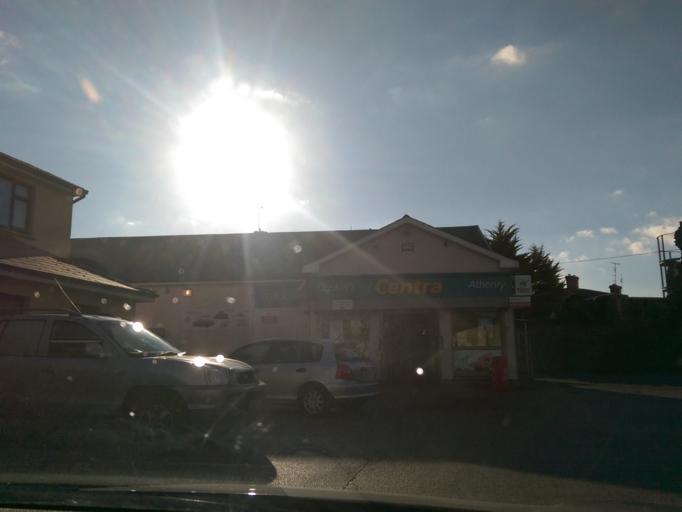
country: IE
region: Connaught
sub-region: County Galway
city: Athenry
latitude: 53.3000
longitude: -8.7471
